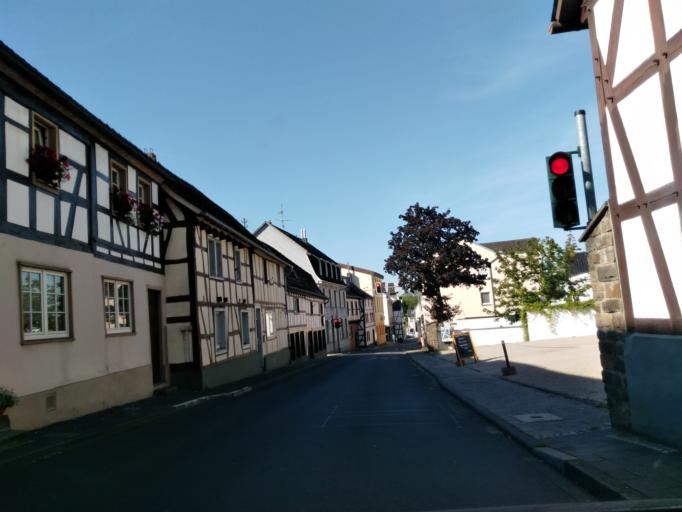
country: DE
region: North Rhine-Westphalia
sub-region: Regierungsbezirk Koln
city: Konigswinter
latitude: 50.6988
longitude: 7.1907
